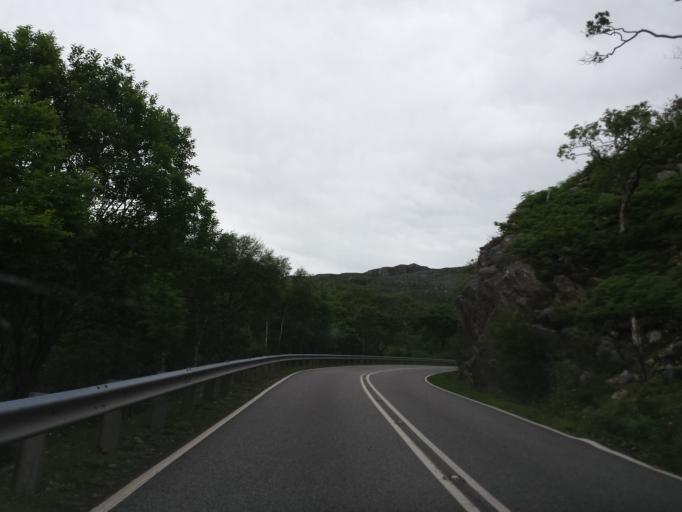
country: GB
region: Scotland
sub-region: Argyll and Bute
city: Isle Of Mull
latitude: 56.8978
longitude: -5.7554
